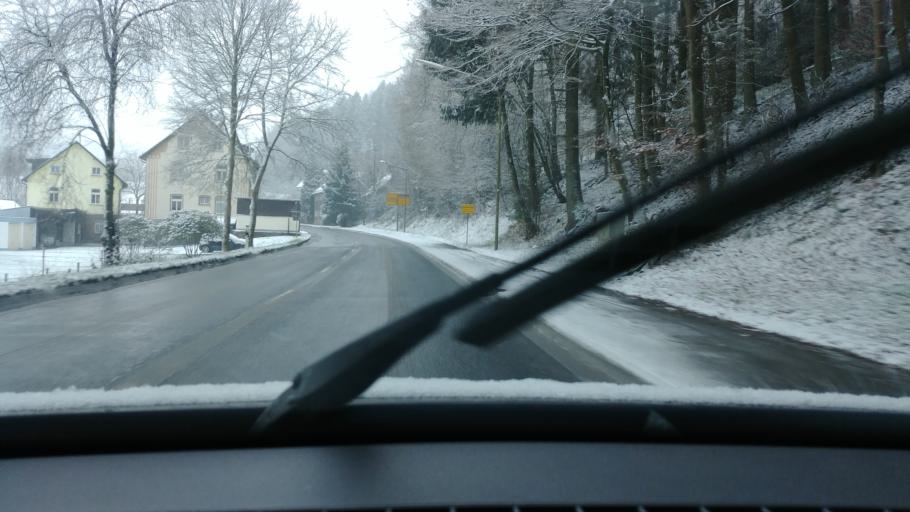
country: DE
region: North Rhine-Westphalia
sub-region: Regierungsbezirk Koln
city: Gummersbach
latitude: 51.0364
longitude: 7.5901
